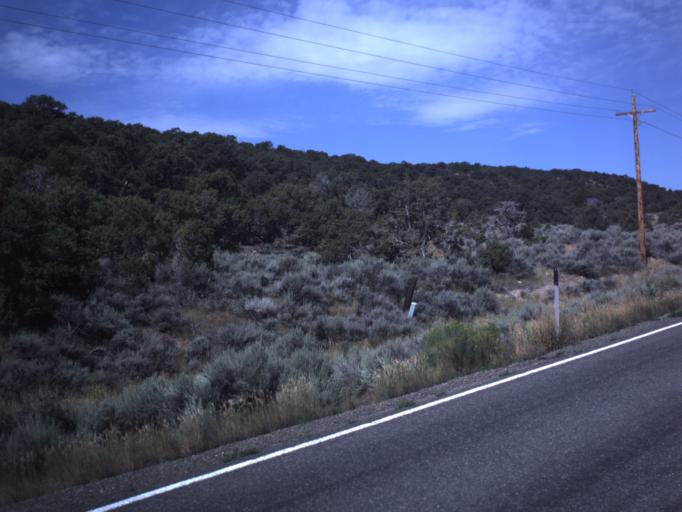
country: US
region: Utah
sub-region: Duchesne County
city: Duchesne
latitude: 40.3212
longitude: -110.3984
